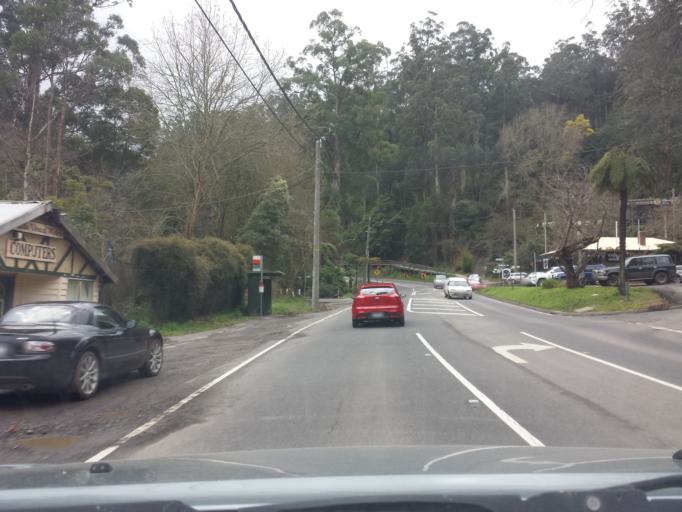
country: AU
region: Victoria
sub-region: Yarra Ranges
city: Belgrave
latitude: -37.9017
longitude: 145.3568
